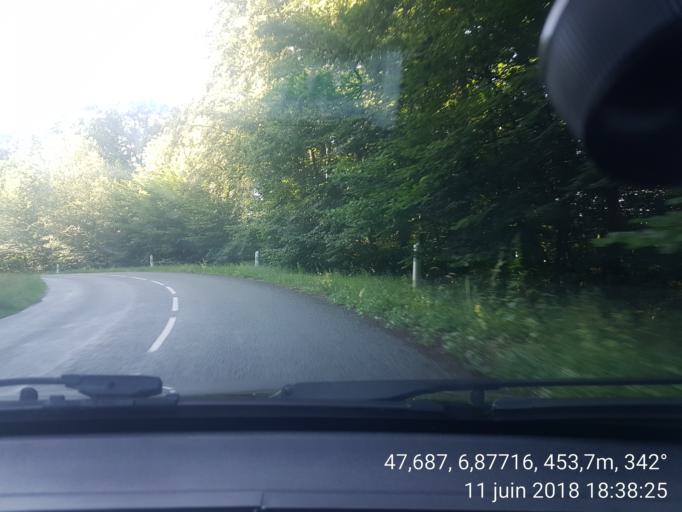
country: FR
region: Franche-Comte
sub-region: Territoire de Belfort
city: Offemont
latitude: 47.6869
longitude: 6.8772
